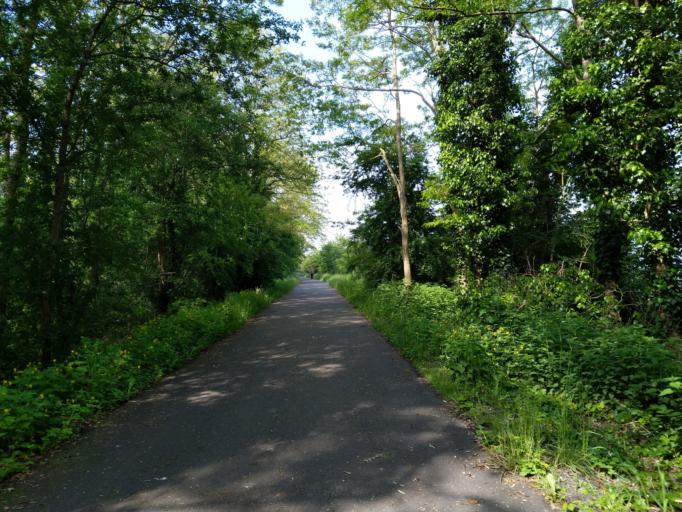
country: BE
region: Wallonia
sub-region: Province du Hainaut
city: Quaregnon
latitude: 50.4307
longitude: 3.8820
